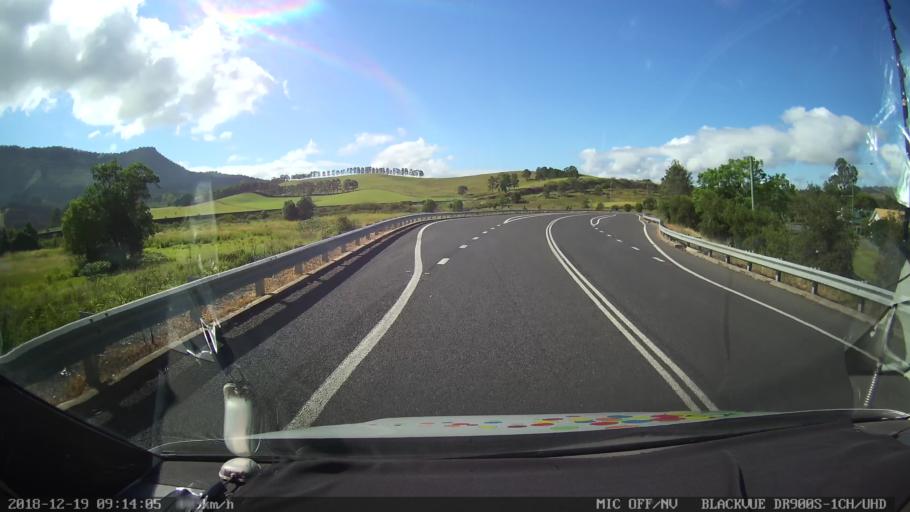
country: AU
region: New South Wales
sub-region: Kyogle
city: Kyogle
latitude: -28.5052
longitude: 152.9672
